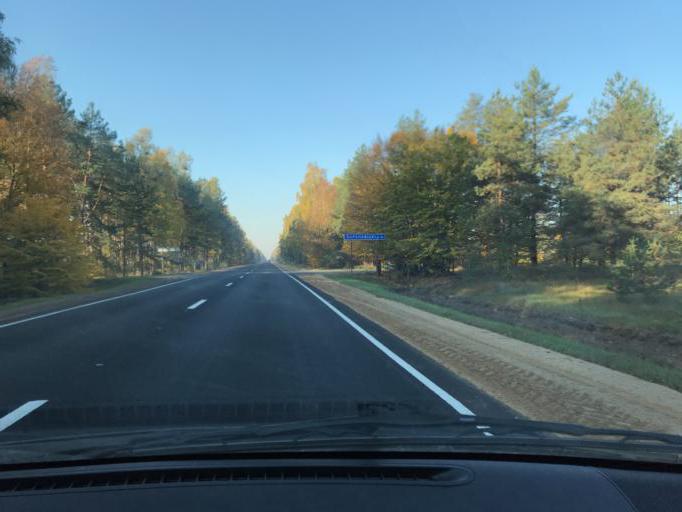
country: BY
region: Brest
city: Baranovichi
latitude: 52.9085
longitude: 25.9154
